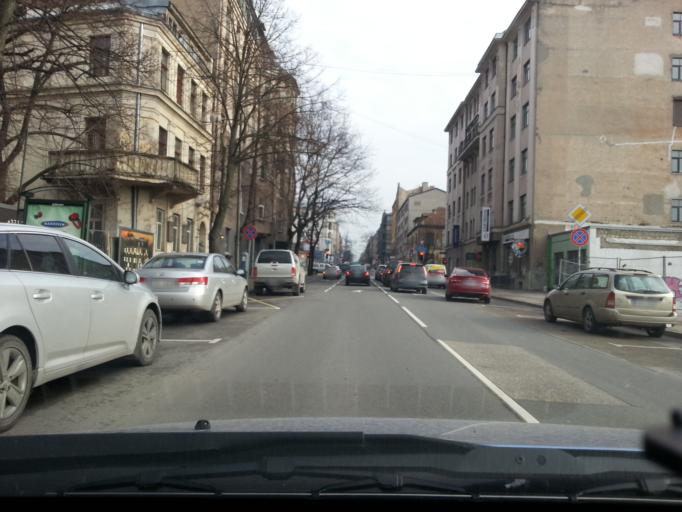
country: LV
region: Riga
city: Riga
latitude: 56.9608
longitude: 24.1193
